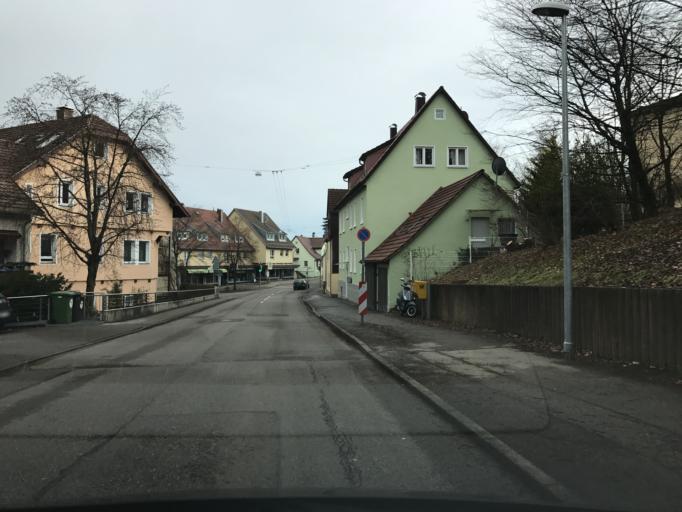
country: DE
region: Baden-Wuerttemberg
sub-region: Regierungsbezirk Stuttgart
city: Ostfildern
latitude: 48.7242
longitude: 9.2061
